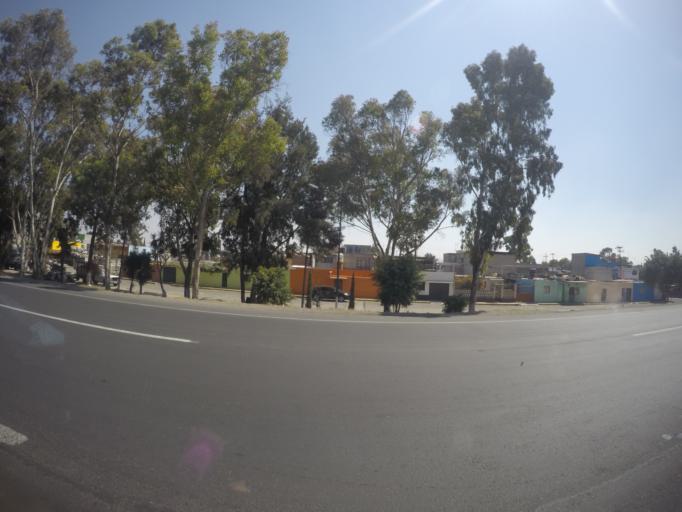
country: MX
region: Mexico
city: Ecatepec
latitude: 19.6040
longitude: -99.0331
